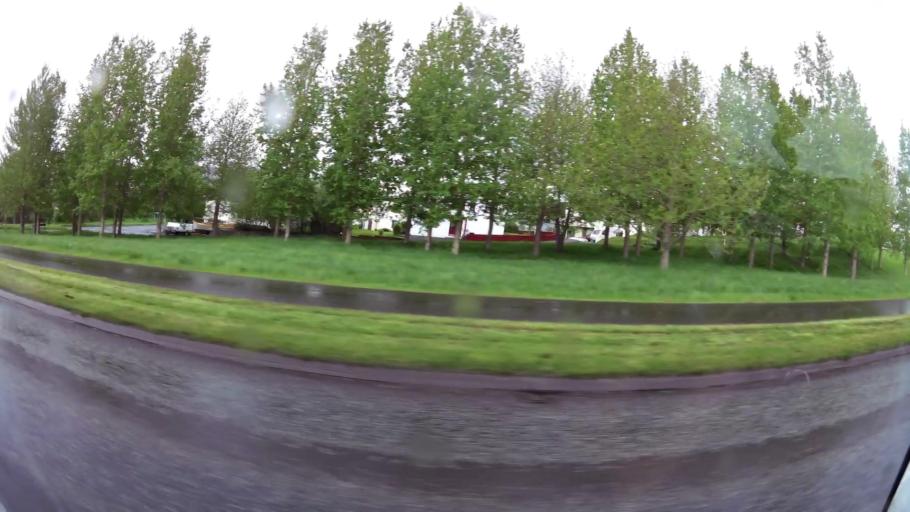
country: IS
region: Northeast
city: Akureyri
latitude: 65.6945
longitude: -18.1087
